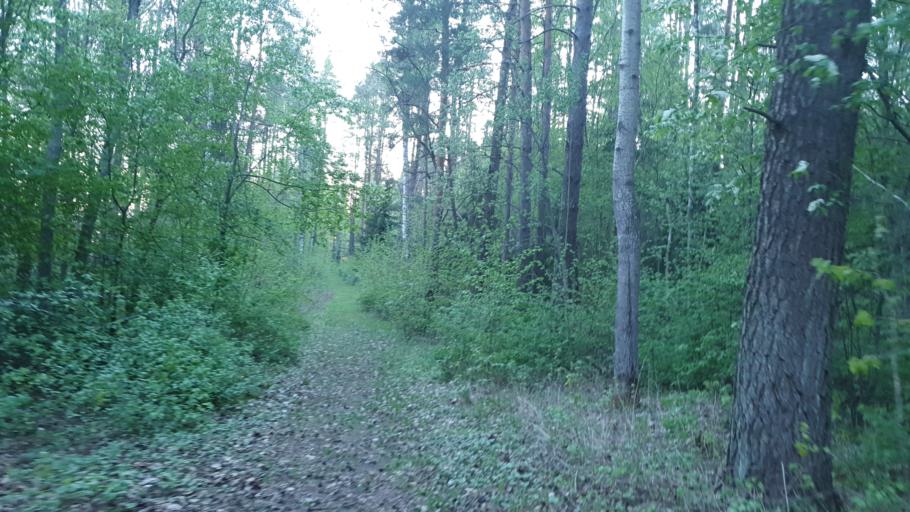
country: LV
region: Ikskile
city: Ikskile
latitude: 56.8340
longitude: 24.4403
